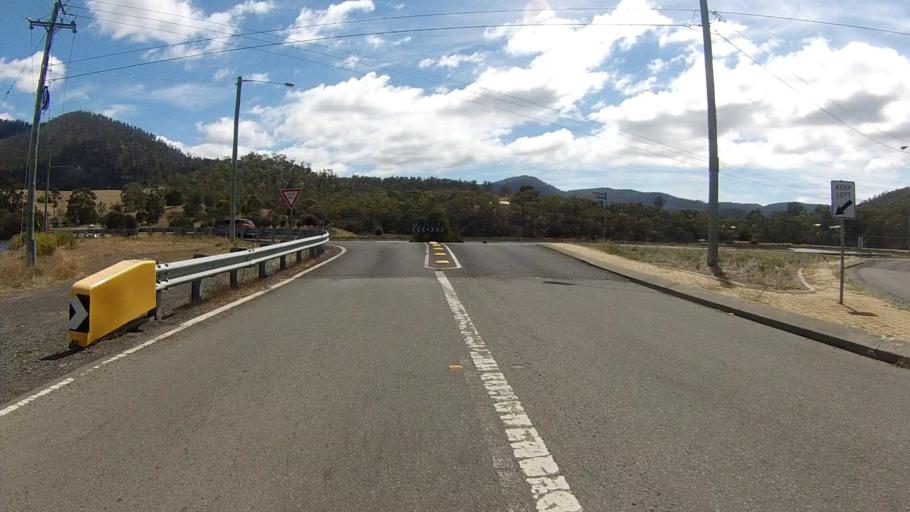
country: AU
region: Tasmania
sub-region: Glenorchy
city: Lutana
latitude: -42.8185
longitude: 147.3208
